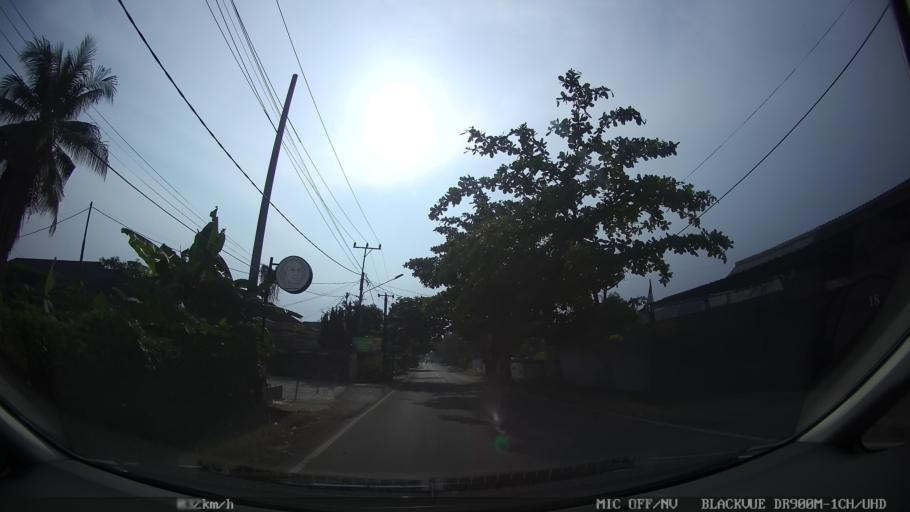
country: ID
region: Lampung
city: Bandarlampung
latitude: -5.4204
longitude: 105.2648
